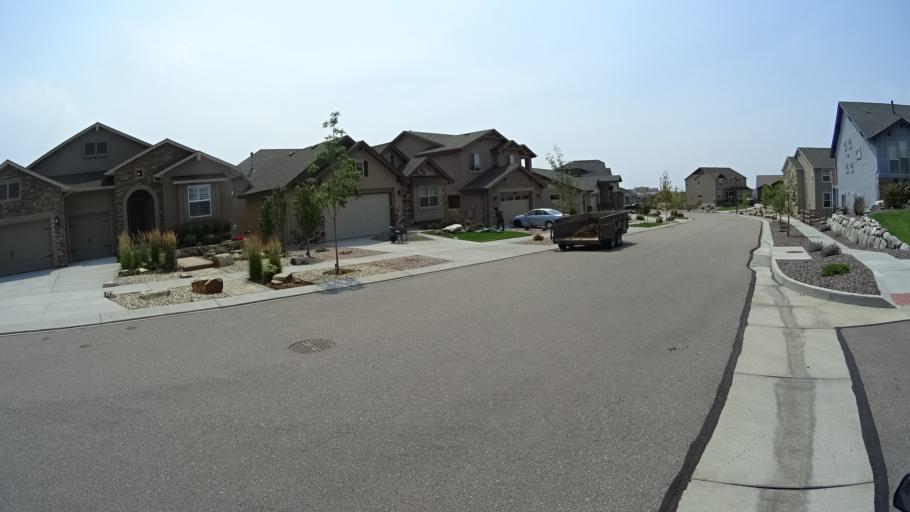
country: US
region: Colorado
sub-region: El Paso County
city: Black Forest
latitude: 38.9652
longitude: -104.7279
